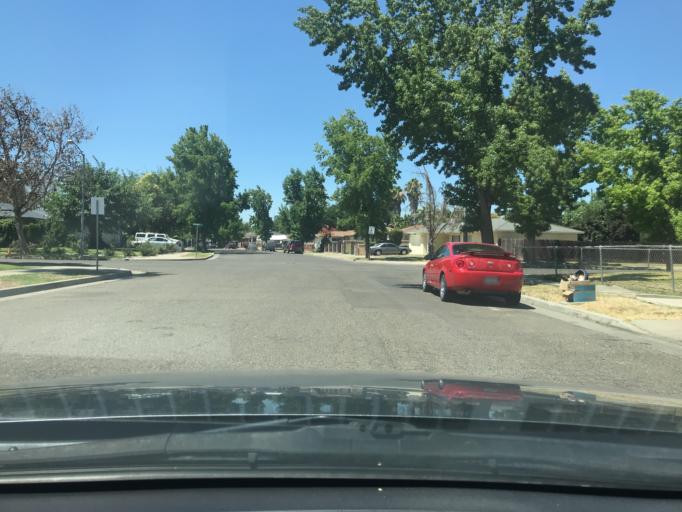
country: US
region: California
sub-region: Merced County
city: Merced
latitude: 37.3224
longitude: -120.4971
